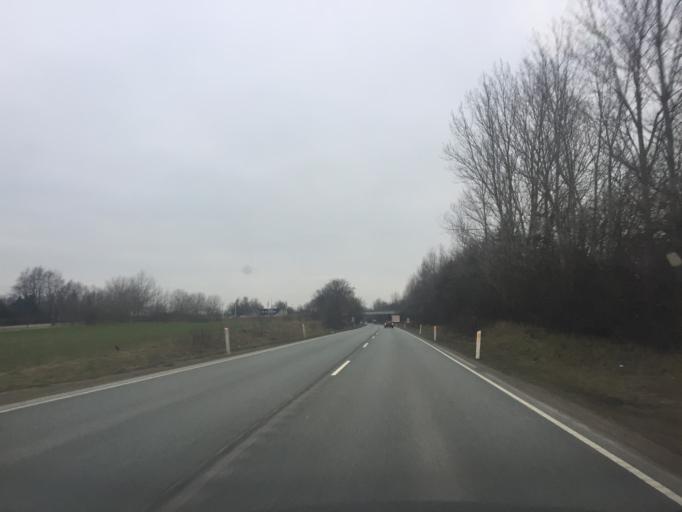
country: DK
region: Capital Region
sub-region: Egedal Kommune
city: Olstykke
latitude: 55.7775
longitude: 12.1525
